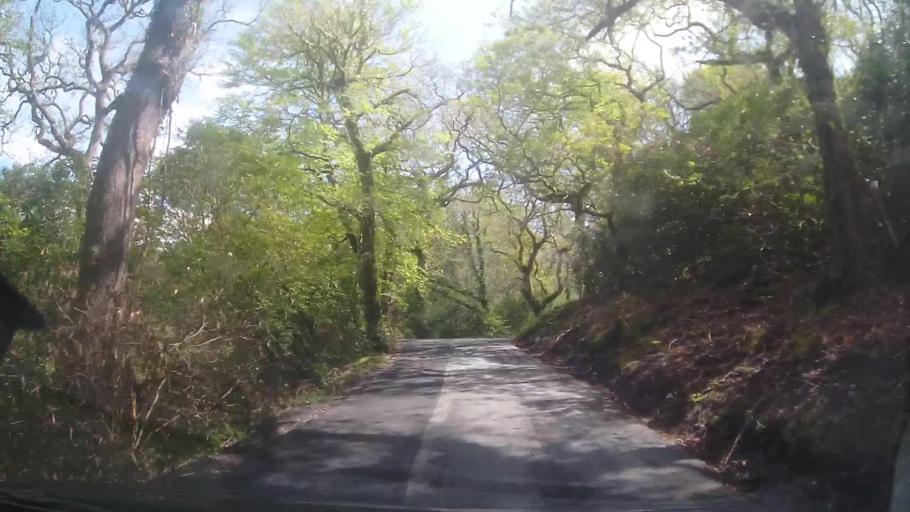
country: GB
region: Wales
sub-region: Gwynedd
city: Porthmadog
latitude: 52.9343
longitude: -4.1724
